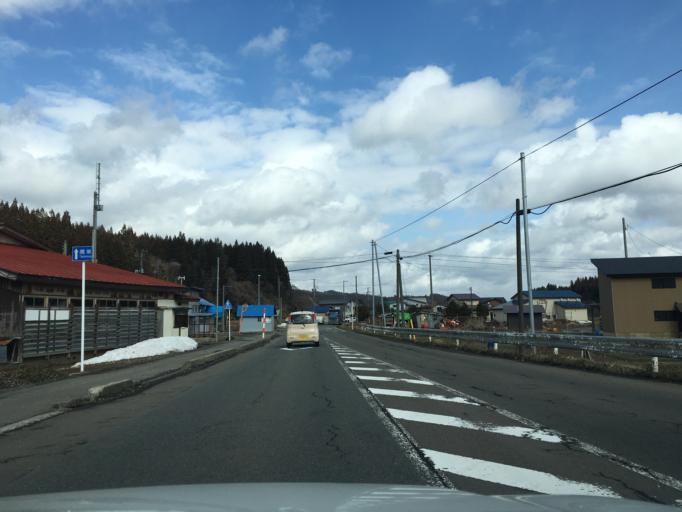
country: JP
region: Akita
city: Takanosu
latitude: 40.0328
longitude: 140.2749
